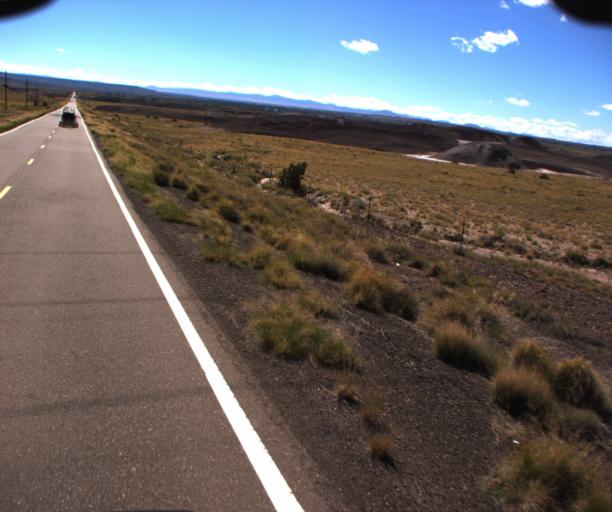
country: US
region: Arizona
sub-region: Apache County
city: Saint Johns
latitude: 34.5563
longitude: -109.3427
